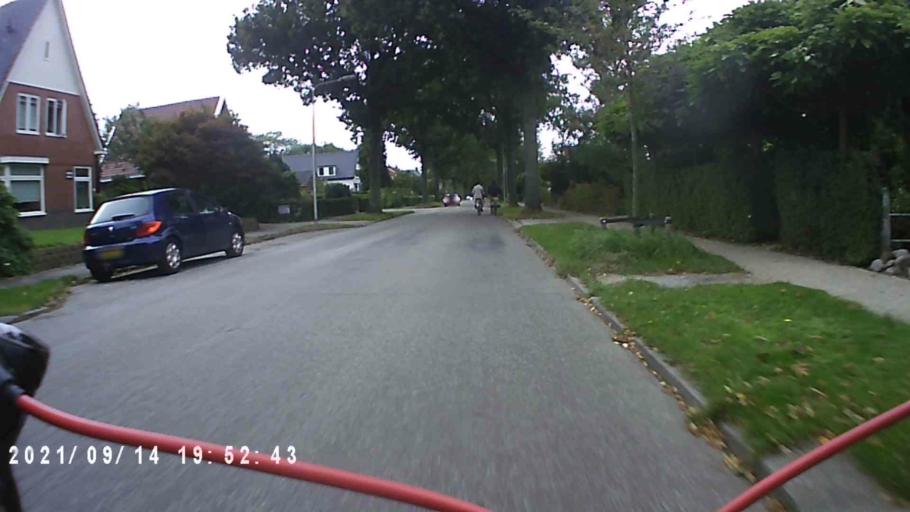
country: NL
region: Groningen
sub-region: Gemeente Haren
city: Haren
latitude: 53.1703
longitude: 6.6198
